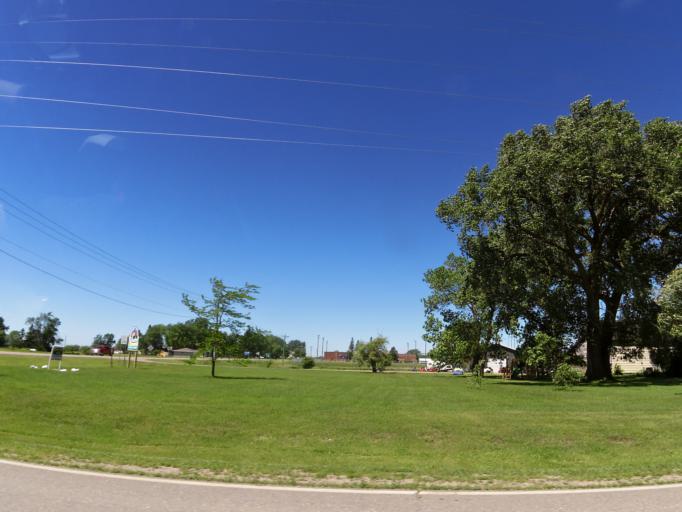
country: US
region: Minnesota
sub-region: Mahnomen County
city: Mahnomen
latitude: 47.1810
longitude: -95.9332
